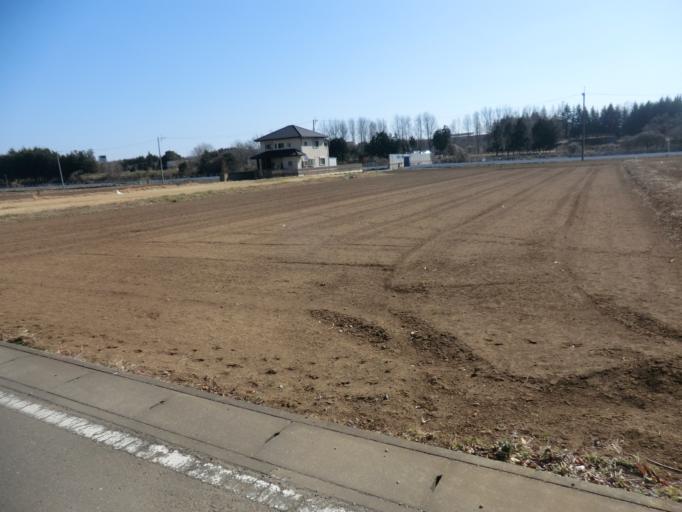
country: JP
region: Ibaraki
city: Naka
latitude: 36.0351
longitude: 140.0911
